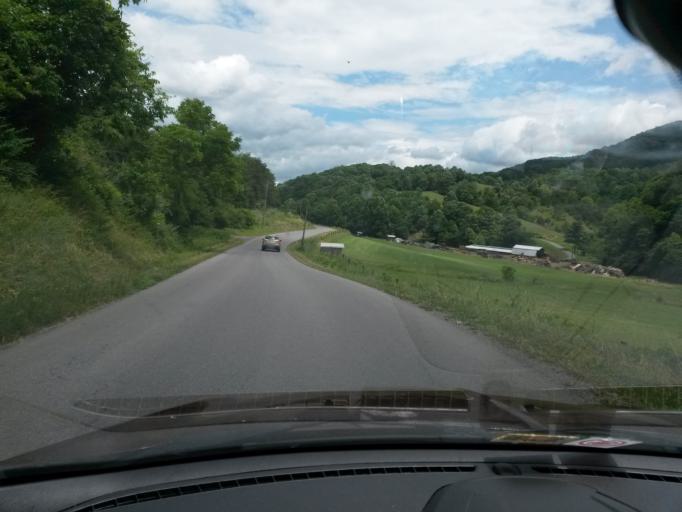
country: US
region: West Virginia
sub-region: Monroe County
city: Union
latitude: 37.5024
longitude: -80.5866
